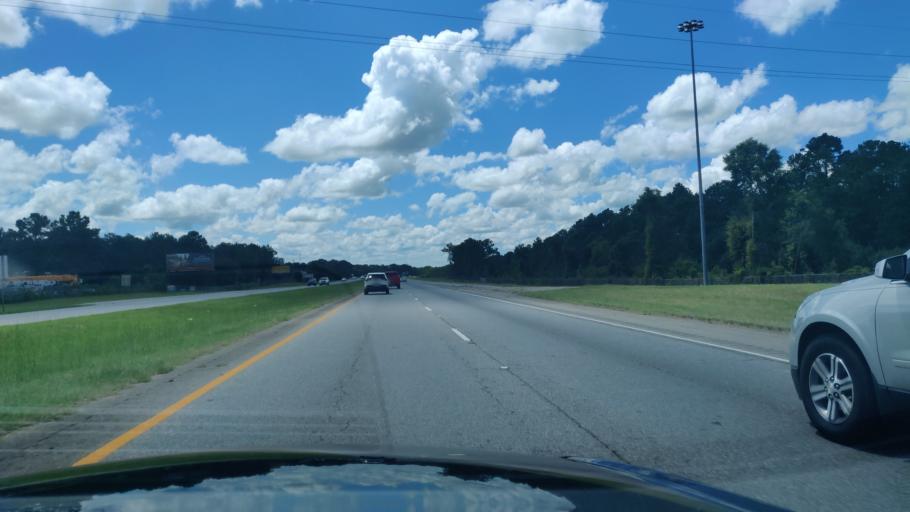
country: US
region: Georgia
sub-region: Dougherty County
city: Albany
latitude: 31.5924
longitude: -84.1270
